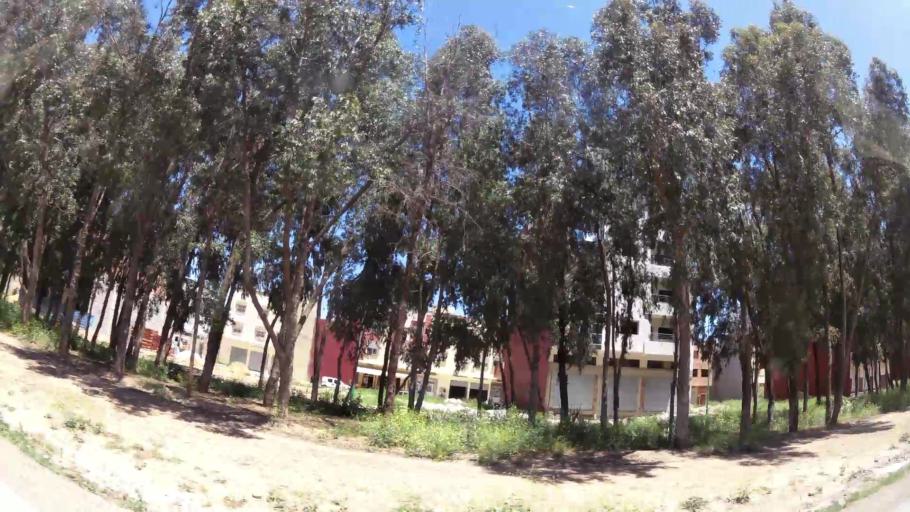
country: MA
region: Meknes-Tafilalet
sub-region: Meknes
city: Meknes
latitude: 33.8544
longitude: -5.5698
